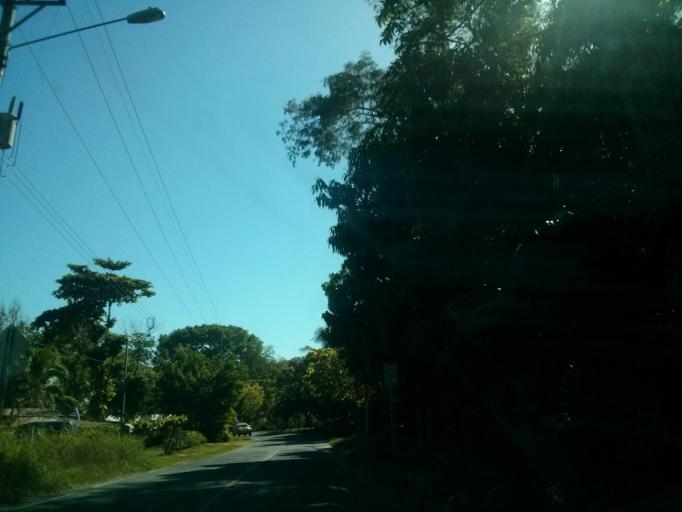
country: CR
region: Puntarenas
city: Paquera
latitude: 9.7757
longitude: -84.9620
